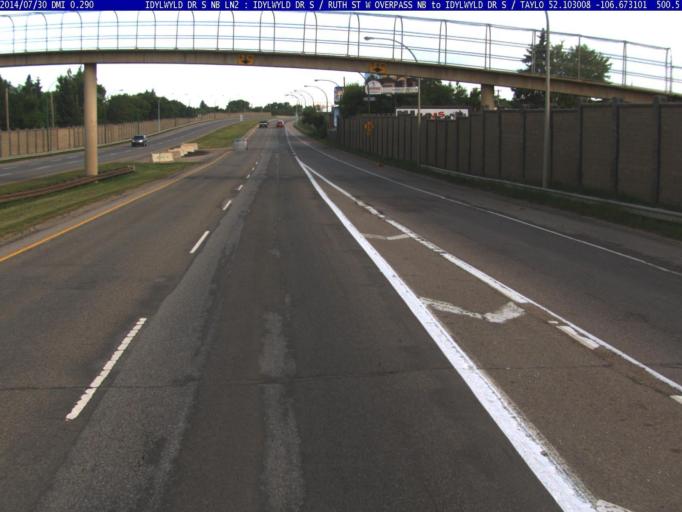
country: CA
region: Saskatchewan
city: Saskatoon
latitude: 52.1030
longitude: -106.6731
